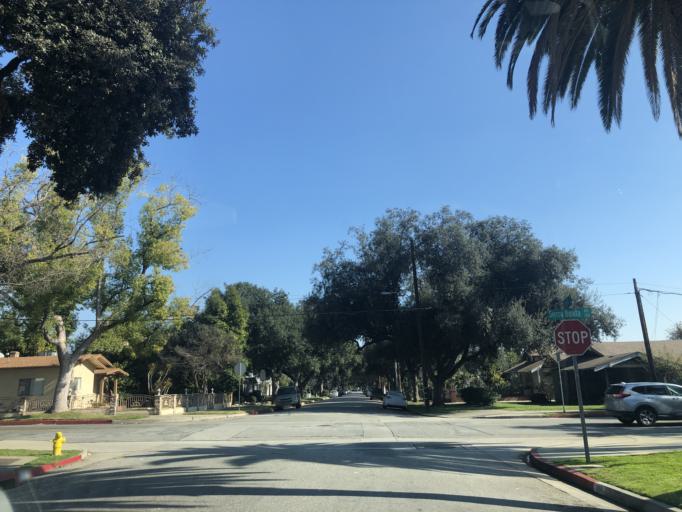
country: US
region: California
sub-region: Los Angeles County
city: East Pasadena
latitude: 34.1508
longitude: -118.1178
